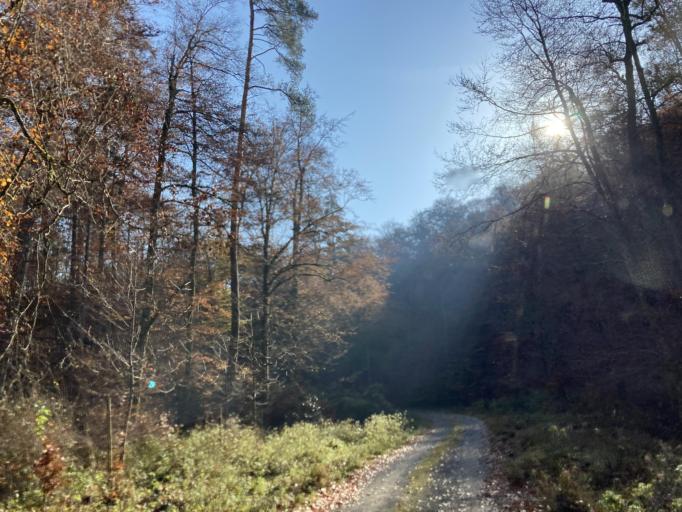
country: DE
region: Baden-Wuerttemberg
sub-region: Regierungsbezirk Stuttgart
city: Altdorf
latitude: 48.5803
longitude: 9.0211
